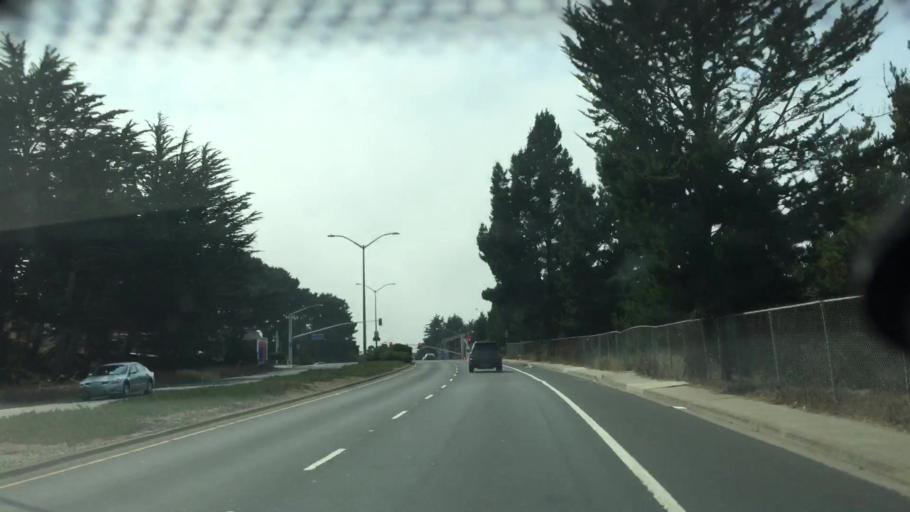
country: US
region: California
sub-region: San Mateo County
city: Colma
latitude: 37.6695
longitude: -122.4734
